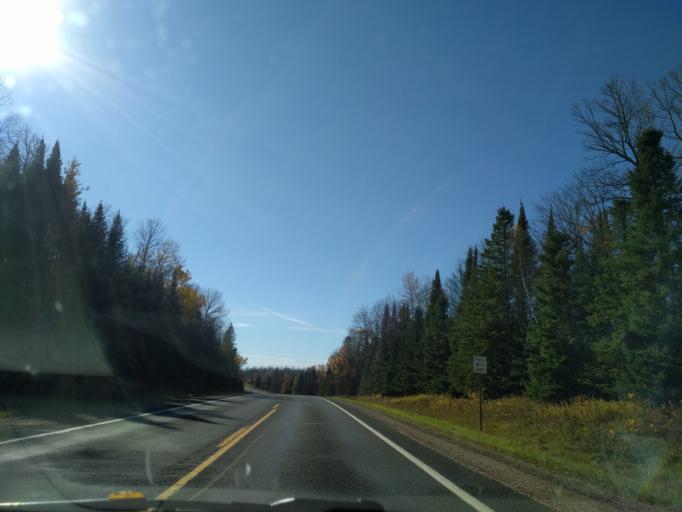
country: US
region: Michigan
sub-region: Iron County
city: Crystal Falls
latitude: 46.1701
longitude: -88.0663
